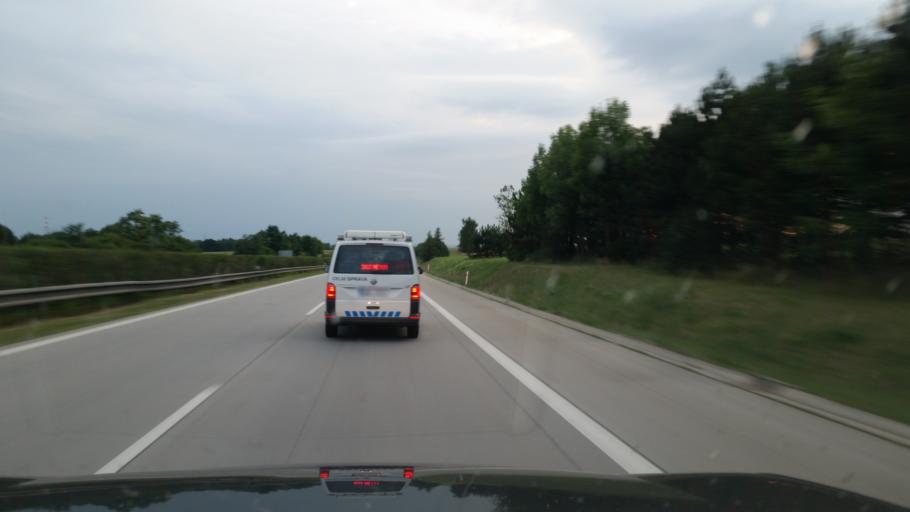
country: CZ
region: Olomoucky
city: Doloplazy
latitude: 49.5840
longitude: 17.4334
